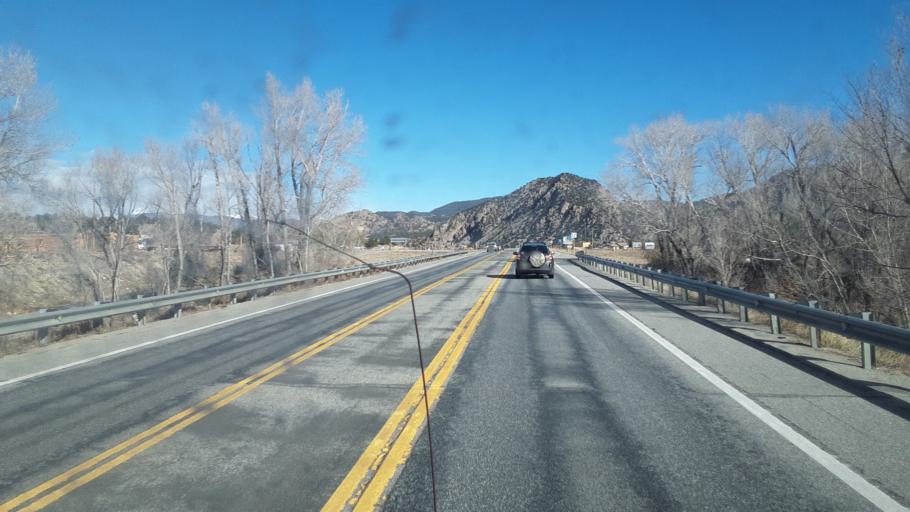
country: US
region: Colorado
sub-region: Chaffee County
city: Buena Vista
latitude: 38.7419
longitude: -106.0827
